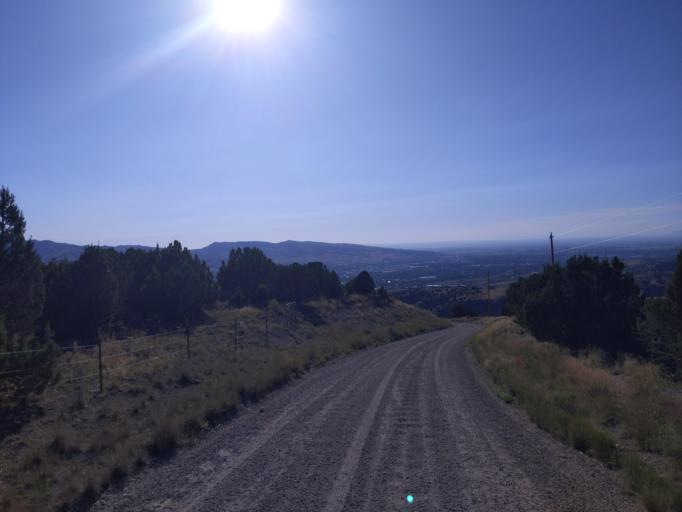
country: US
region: Idaho
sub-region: Bannock County
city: Pocatello
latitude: 42.8532
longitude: -112.3822
